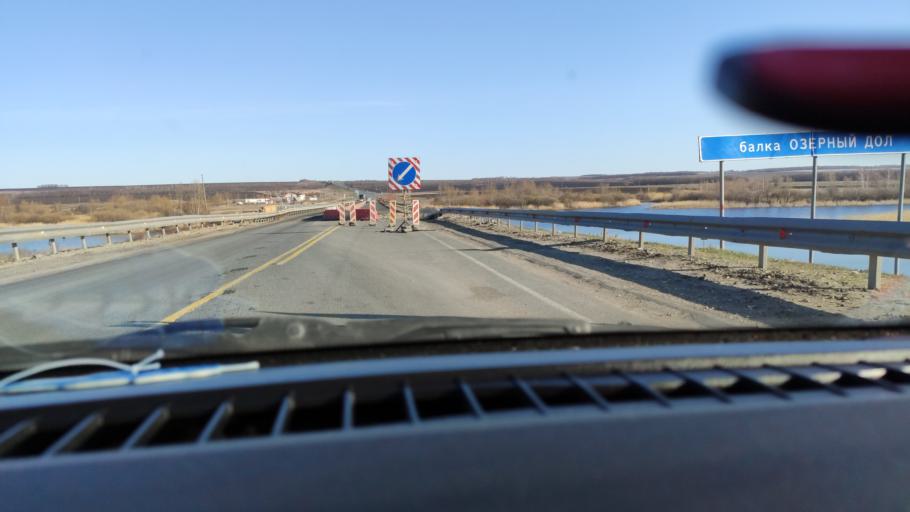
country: RU
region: Saratov
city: Dukhovnitskoye
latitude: 52.7364
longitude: 48.2561
